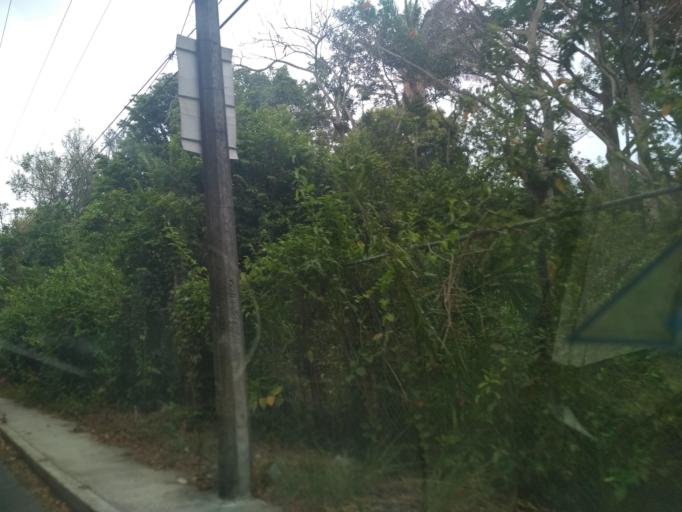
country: MX
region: Veracruz
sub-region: Medellin
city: Fraccionamiento Arboledas San Ramon
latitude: 19.0920
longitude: -96.1425
